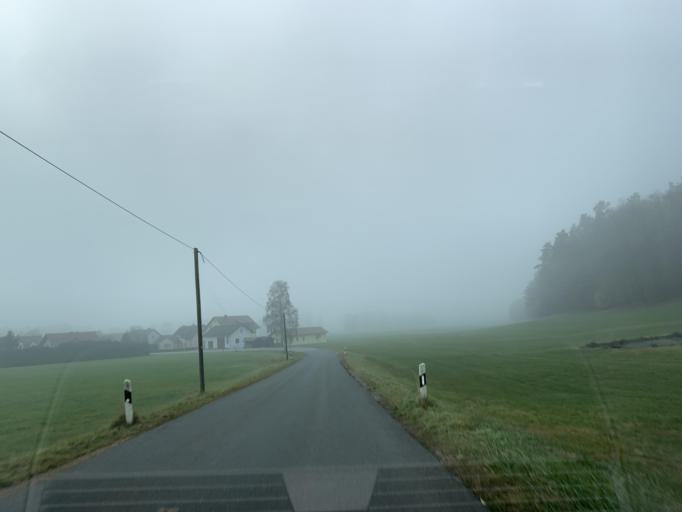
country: DE
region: Bavaria
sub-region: Upper Palatinate
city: Neunburg vorm Wald
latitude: 49.3653
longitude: 12.3943
